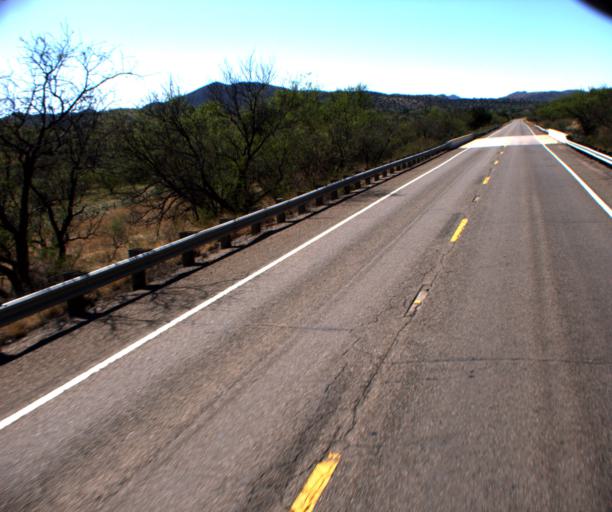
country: US
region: Arizona
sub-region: Santa Cruz County
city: Rio Rico
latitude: 31.6427
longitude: -110.7146
